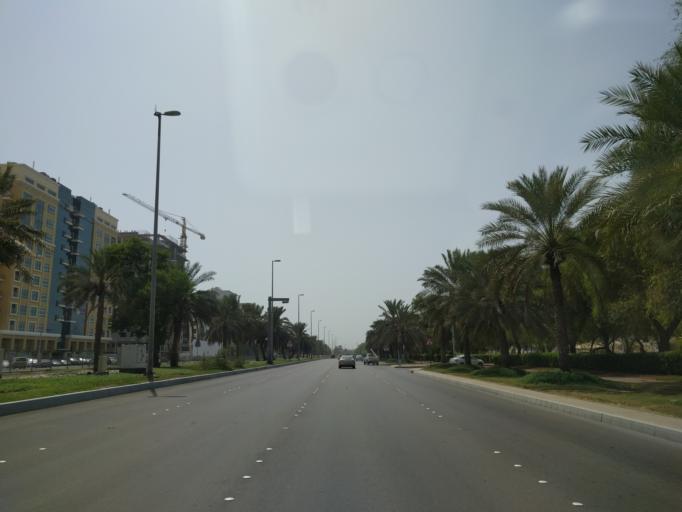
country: AE
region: Abu Dhabi
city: Abu Dhabi
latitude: 24.4394
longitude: 54.4124
